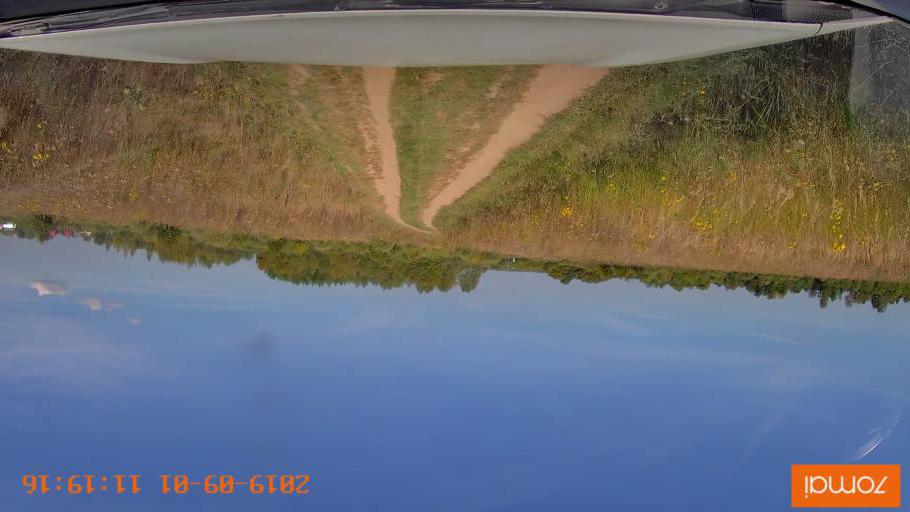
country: RU
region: Kaluga
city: Detchino
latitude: 54.8278
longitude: 36.3632
